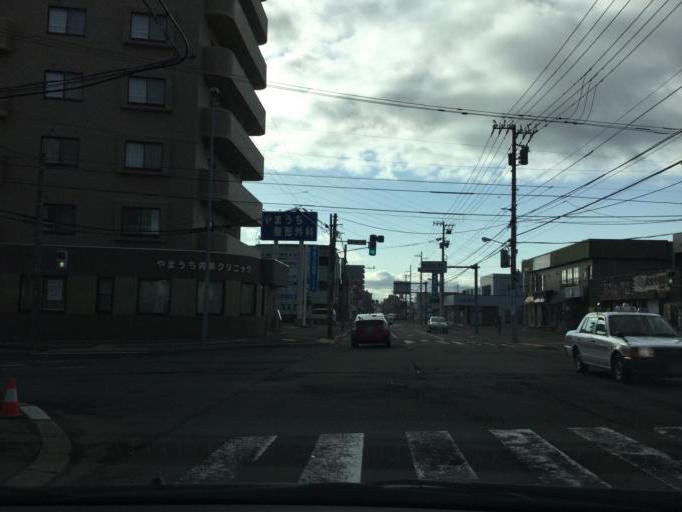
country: JP
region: Hokkaido
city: Sapporo
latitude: 43.0260
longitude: 141.4339
